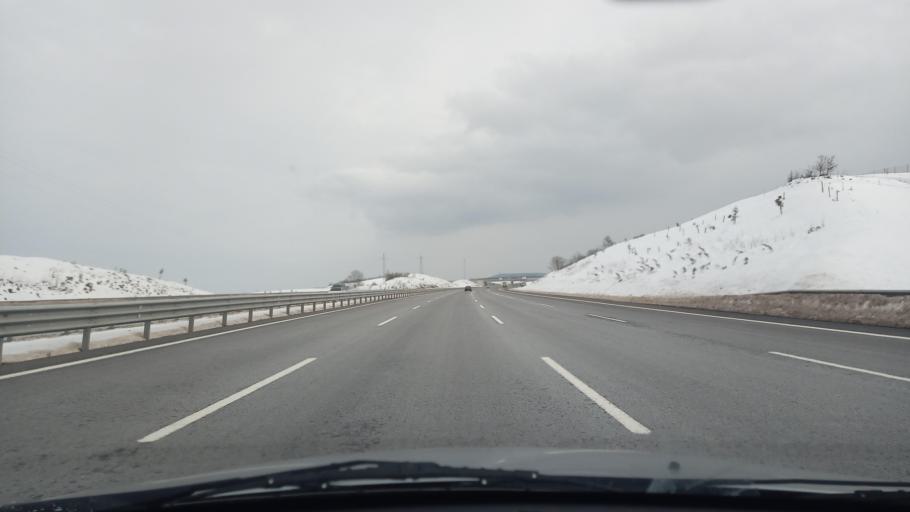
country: TR
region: Kocaeli
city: Derince
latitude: 40.8637
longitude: 29.8367
